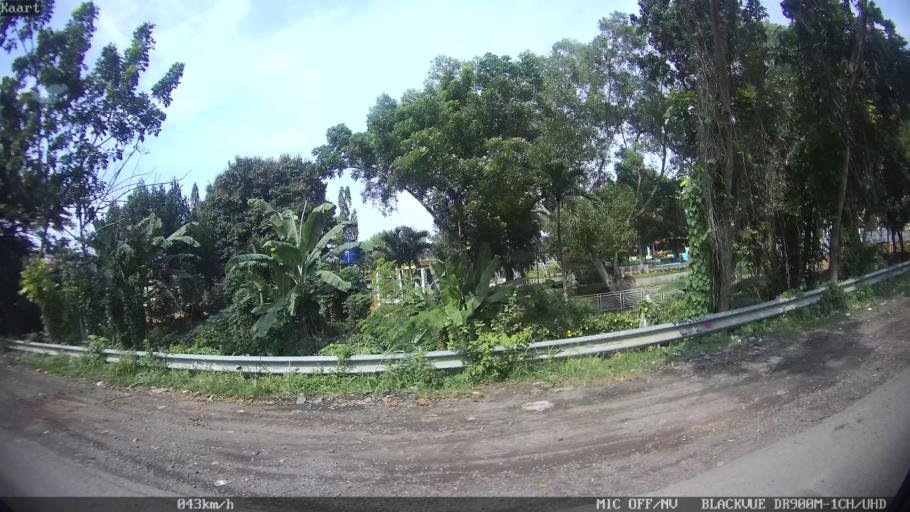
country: ID
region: Lampung
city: Kedaton
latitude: -5.3776
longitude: 105.2811
